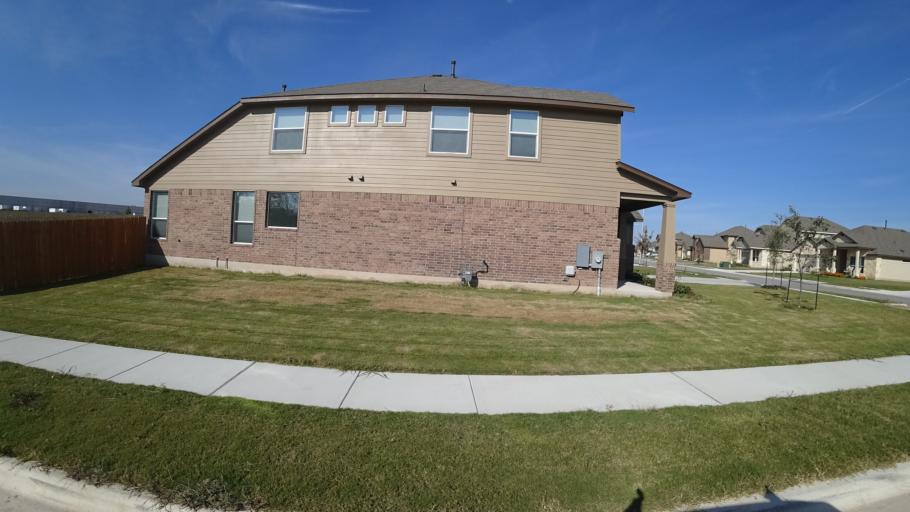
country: US
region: Texas
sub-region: Travis County
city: Pflugerville
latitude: 30.4093
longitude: -97.6418
